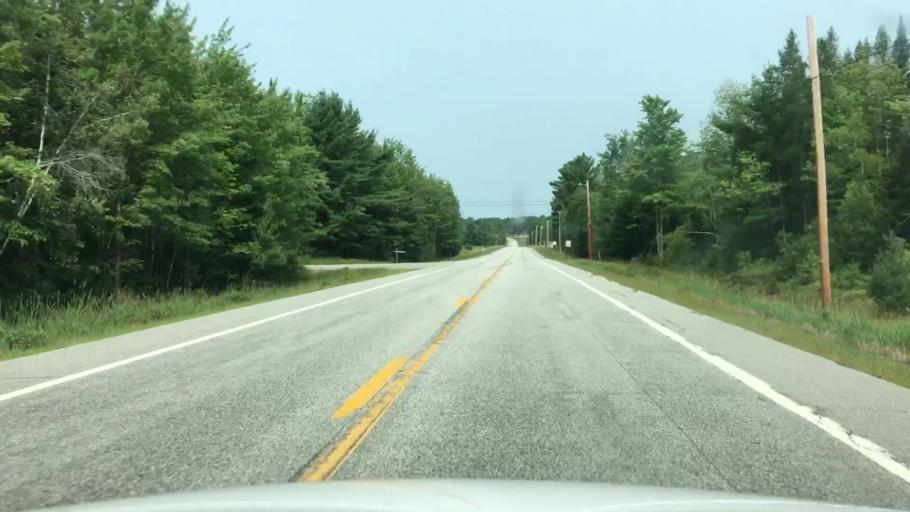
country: US
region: Maine
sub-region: Kennebec County
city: Wayne
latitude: 44.3870
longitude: -70.1092
